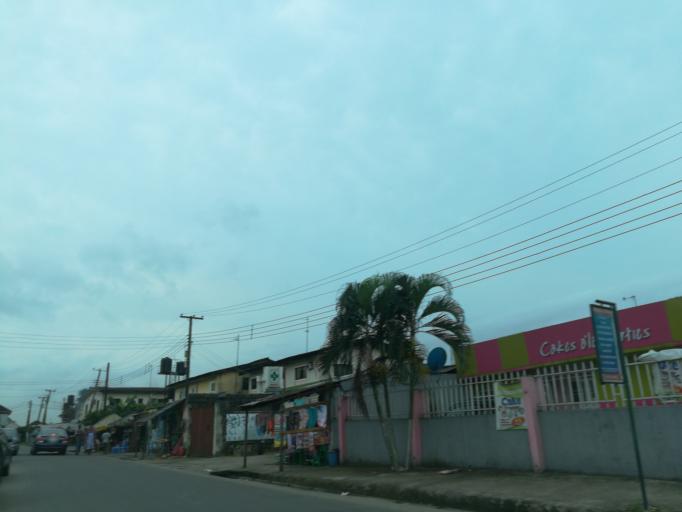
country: NG
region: Rivers
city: Port Harcourt
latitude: 4.8217
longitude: 7.0251
